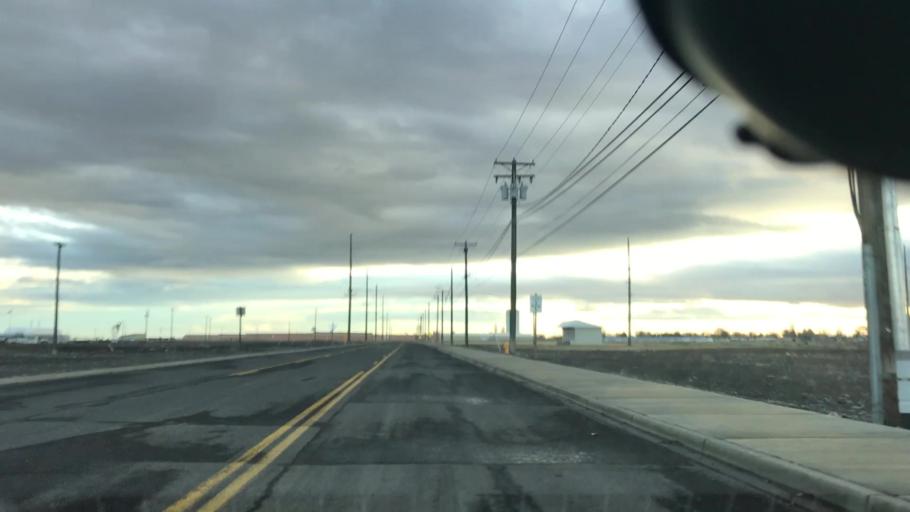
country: US
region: Washington
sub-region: Grant County
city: Moses Lake North
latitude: 47.1820
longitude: -119.3166
